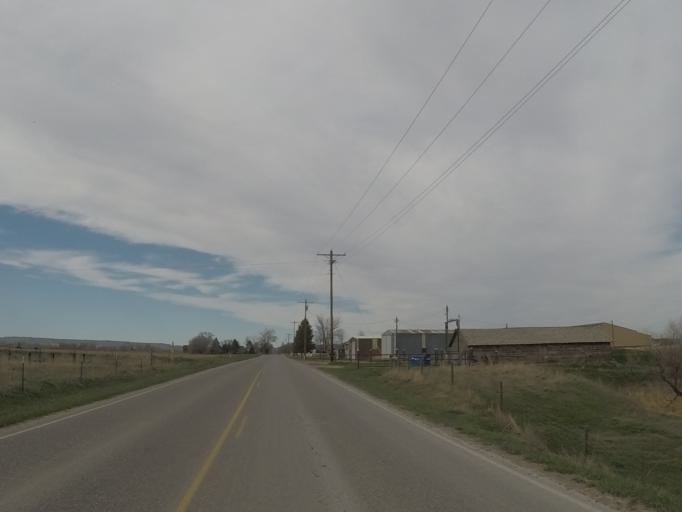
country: US
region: Montana
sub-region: Yellowstone County
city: Laurel
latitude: 45.7183
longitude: -108.6587
